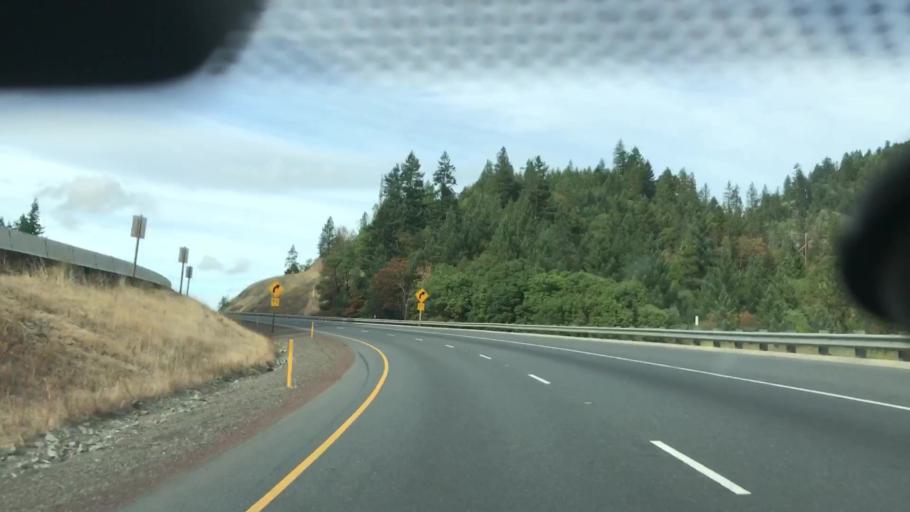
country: US
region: Oregon
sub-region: Josephine County
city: Merlin
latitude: 42.6565
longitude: -123.3757
